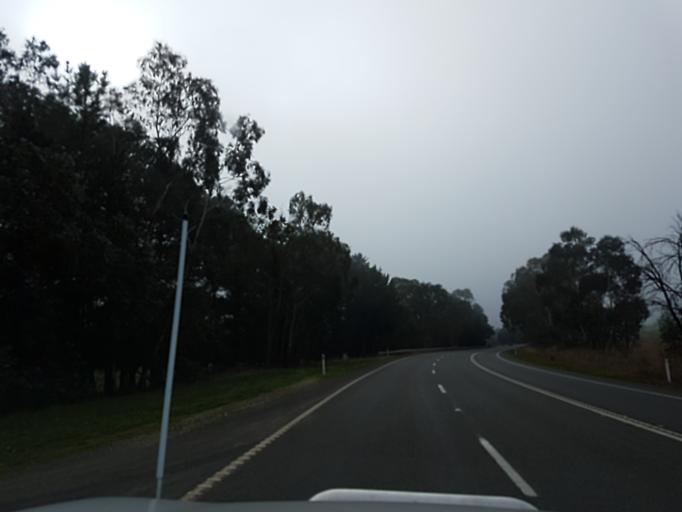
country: AU
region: Victoria
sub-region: Murrindindi
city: Kinglake West
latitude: -37.3160
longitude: 145.4508
